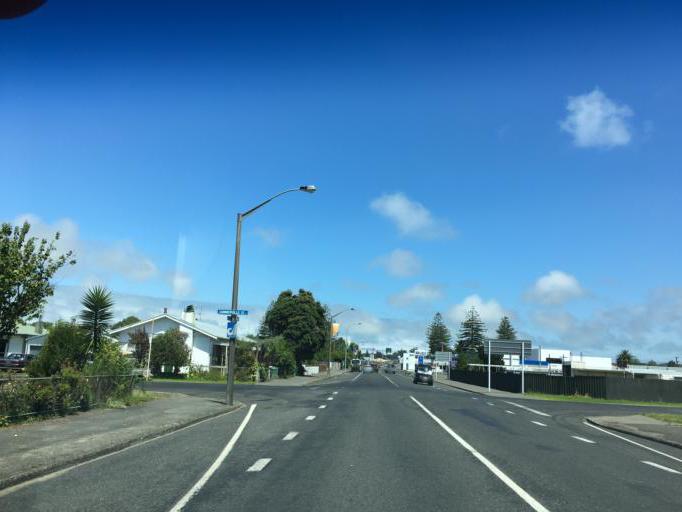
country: NZ
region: Hawke's Bay
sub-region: Wairoa District
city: Wairoa
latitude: -39.0280
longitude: 177.4192
